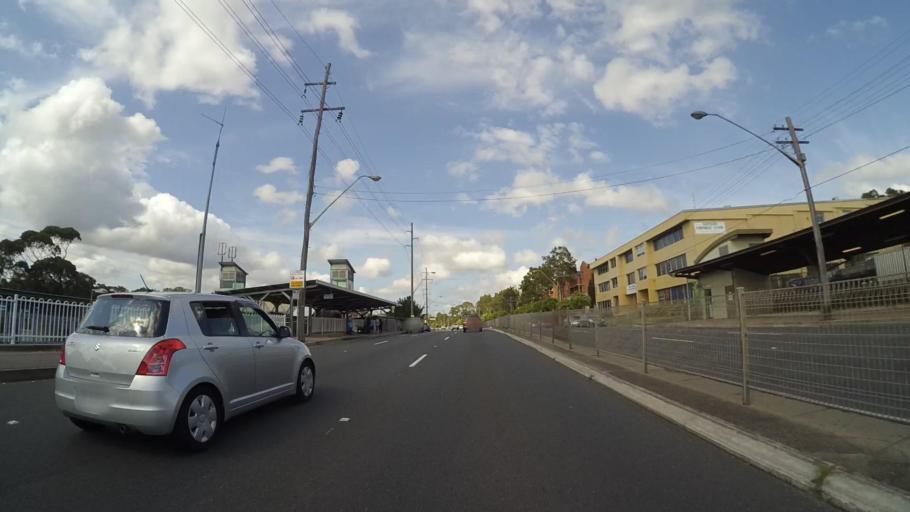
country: AU
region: New South Wales
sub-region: Sutherland Shire
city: Engadine
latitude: -34.0673
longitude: 151.0148
